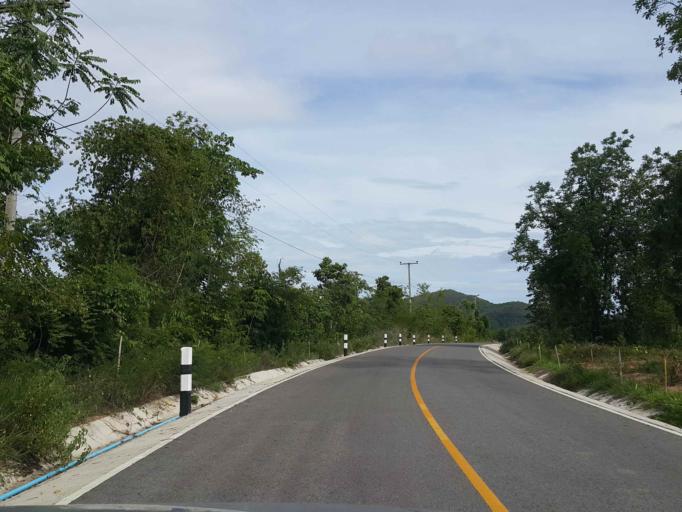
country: TH
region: Sukhothai
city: Thung Saliam
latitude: 17.2343
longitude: 99.5081
